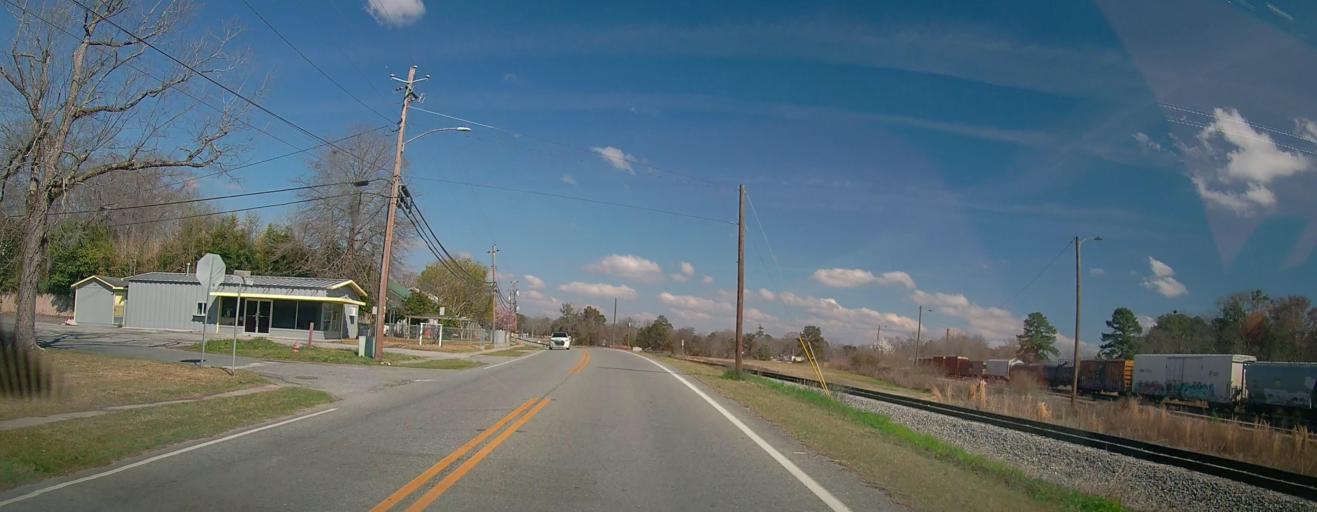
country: US
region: Georgia
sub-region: Wilkinson County
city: Gordon
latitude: 32.8823
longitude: -83.3303
